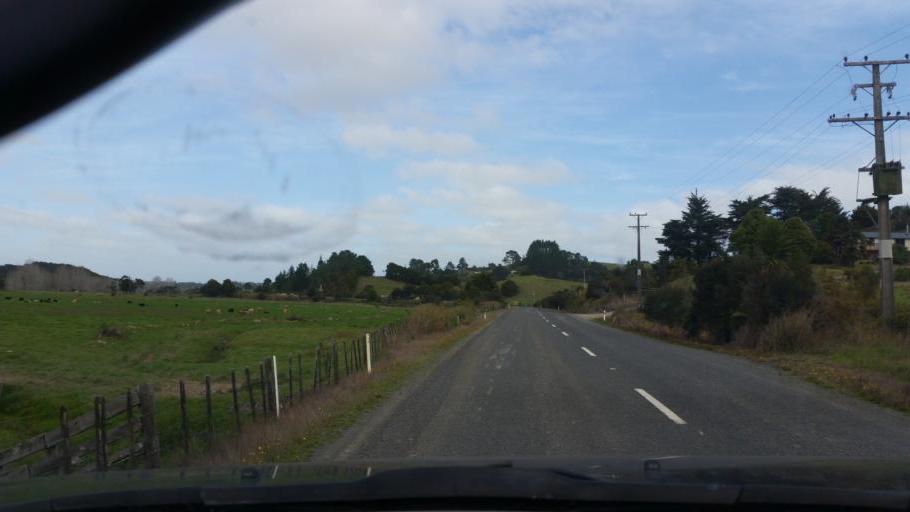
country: NZ
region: Northland
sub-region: Kaipara District
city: Dargaville
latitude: -35.8868
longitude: 173.8416
